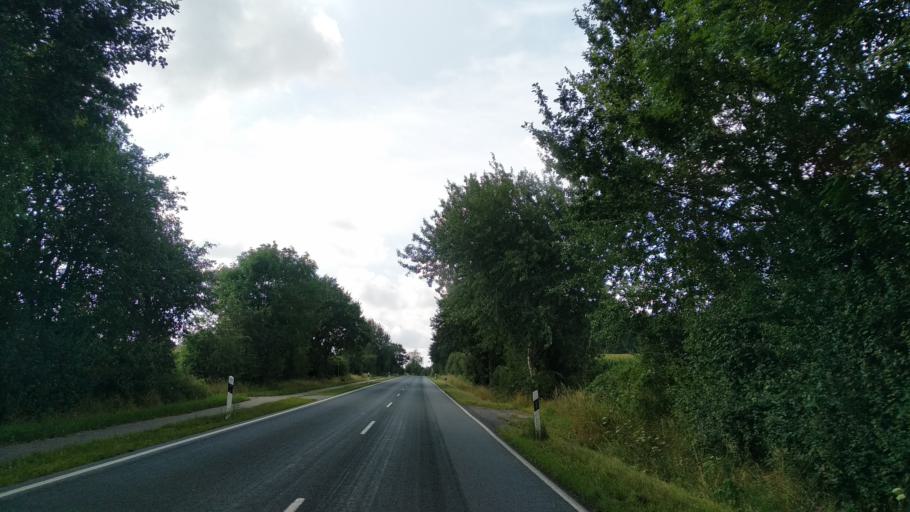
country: DE
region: Schleswig-Holstein
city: Selk
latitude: 54.4812
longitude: 9.5654
